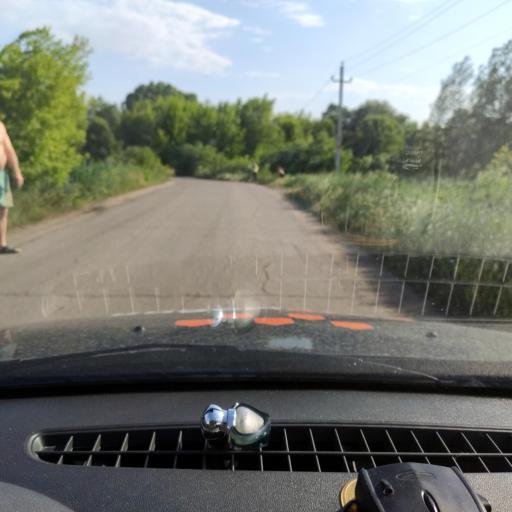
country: RU
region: Voronezj
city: Podkletnoye
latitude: 51.6190
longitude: 39.4408
